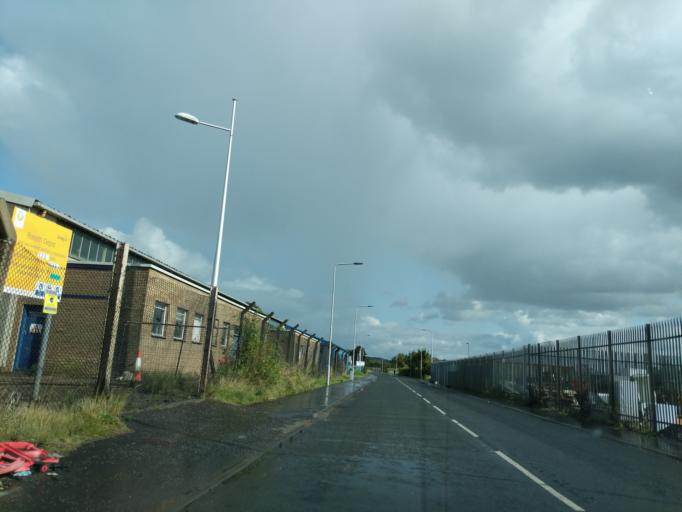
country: GB
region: Scotland
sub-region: Fife
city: Rosyth
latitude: 56.0249
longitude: -3.4332
